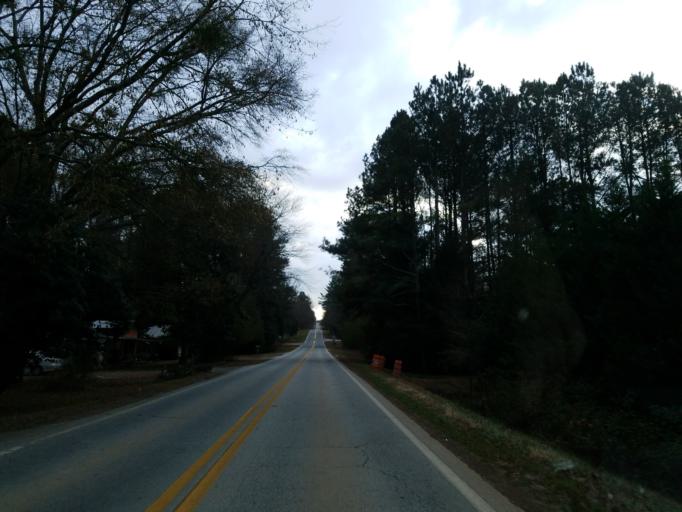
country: US
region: Georgia
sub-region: Dawson County
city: Dawsonville
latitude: 34.3354
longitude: -84.0659
